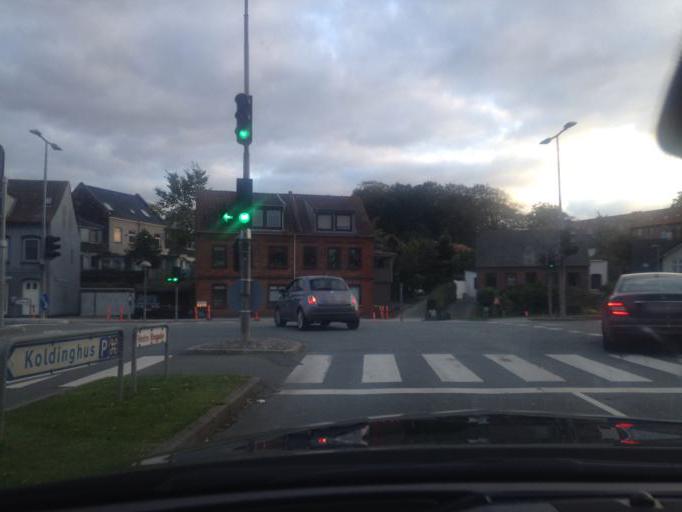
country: DK
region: South Denmark
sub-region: Kolding Kommune
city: Kolding
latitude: 55.4869
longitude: 9.4643
